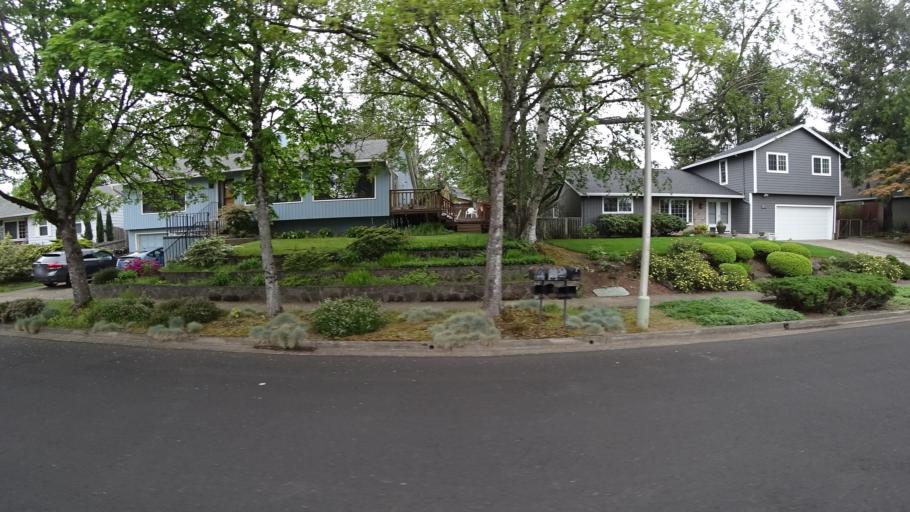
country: US
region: Oregon
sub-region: Washington County
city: Beaverton
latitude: 45.4545
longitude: -122.8239
